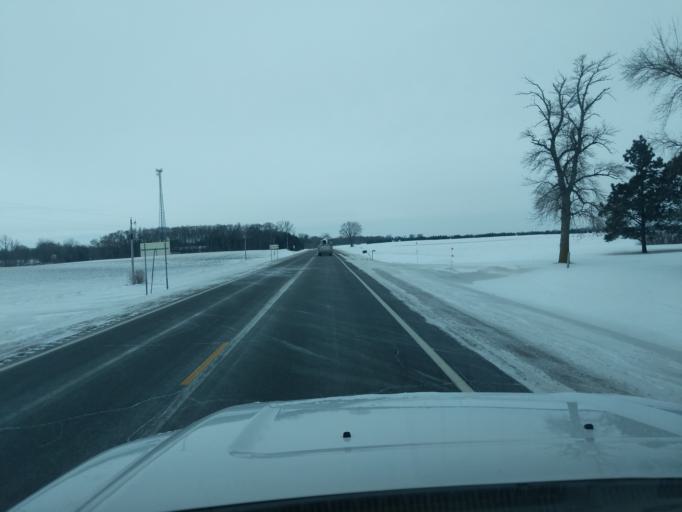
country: US
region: Minnesota
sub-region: Redwood County
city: Redwood Falls
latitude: 44.5761
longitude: -94.9946
